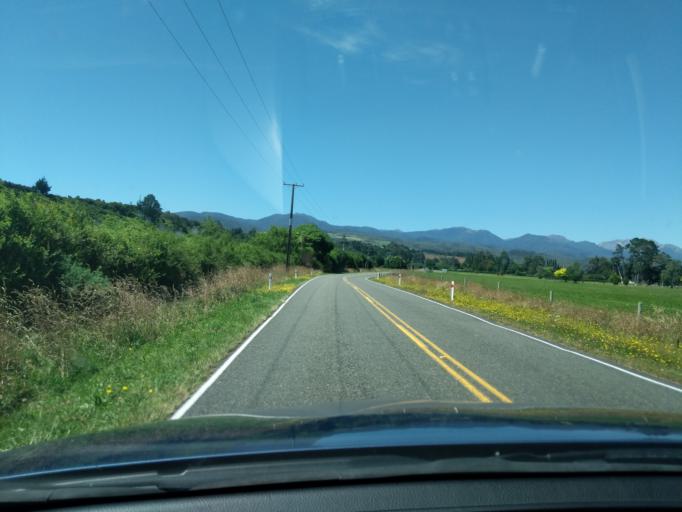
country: NZ
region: Tasman
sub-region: Tasman District
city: Takaka
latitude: -40.7153
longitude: 172.6382
